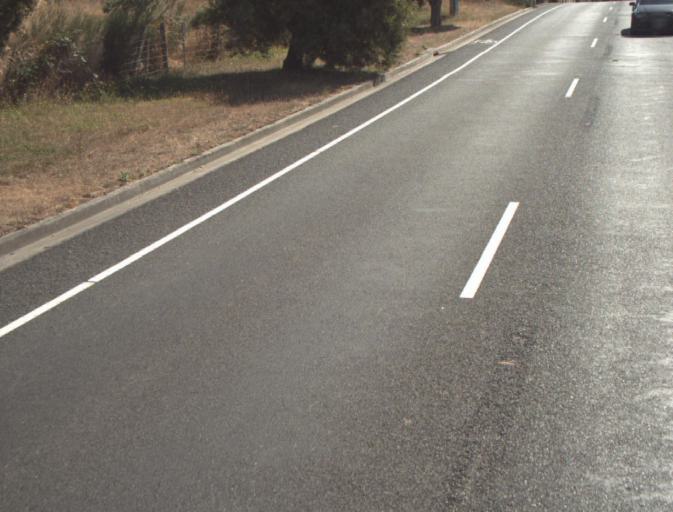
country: AU
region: Tasmania
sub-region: Launceston
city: Newstead
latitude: -41.4303
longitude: 147.1739
